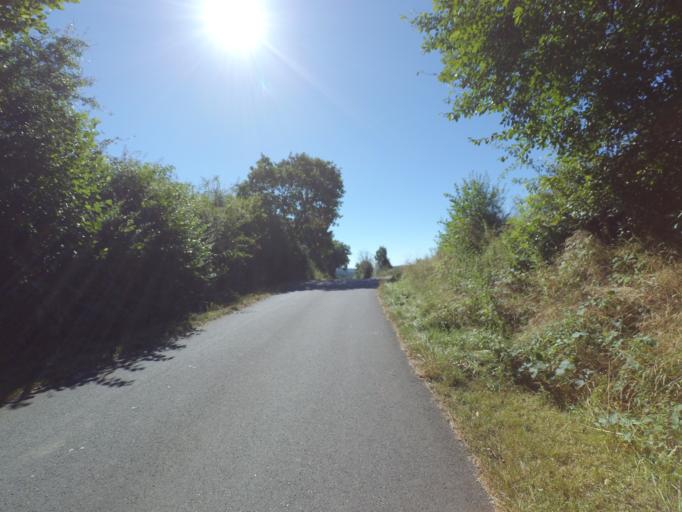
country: DE
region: Rheinland-Pfalz
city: Schonbach
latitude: 50.2121
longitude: 6.9502
